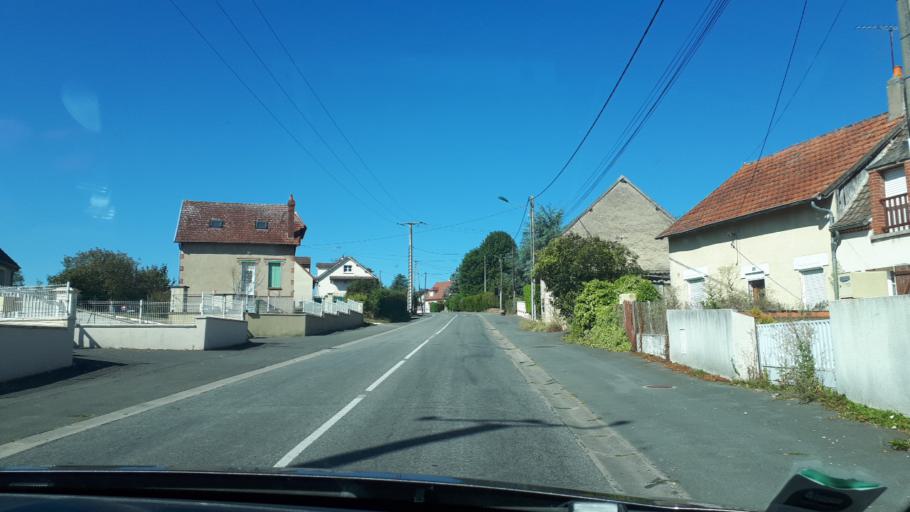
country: FR
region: Centre
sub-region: Departement du Loiret
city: Briare
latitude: 47.5878
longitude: 2.7397
